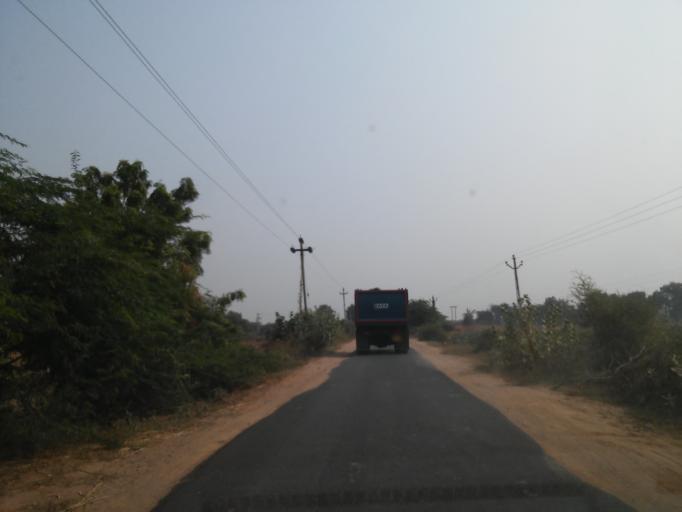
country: IN
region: Gujarat
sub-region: Kachchh
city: Bhuj
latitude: 23.4316
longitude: 69.6952
